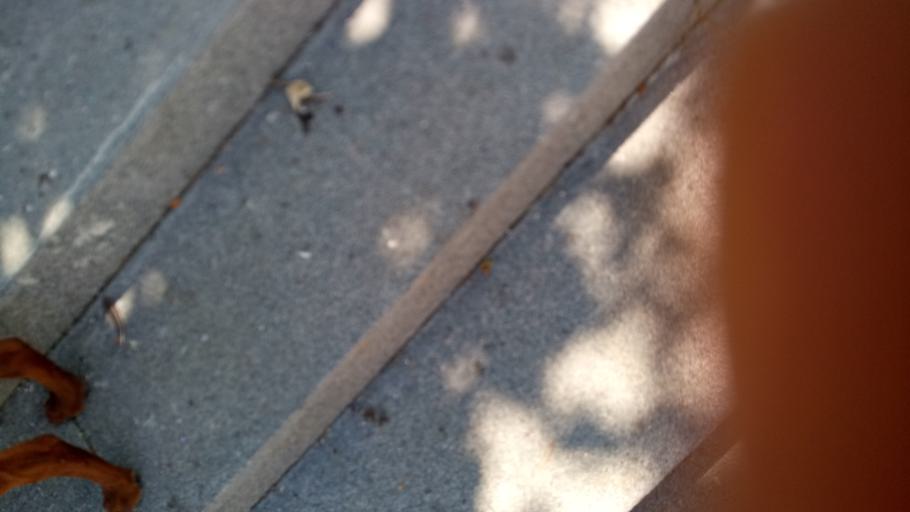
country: PT
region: Evora
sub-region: Arraiolos
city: Arraiolos
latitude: 38.7236
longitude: -7.9843
